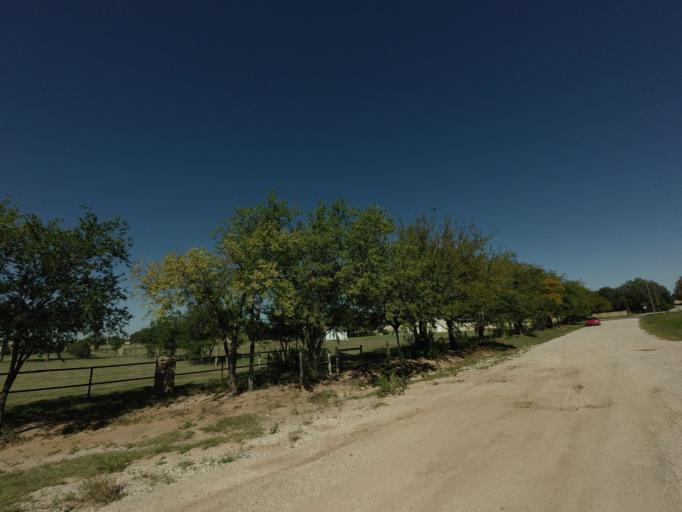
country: US
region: New Mexico
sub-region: Curry County
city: Clovis
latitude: 34.4326
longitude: -103.1876
